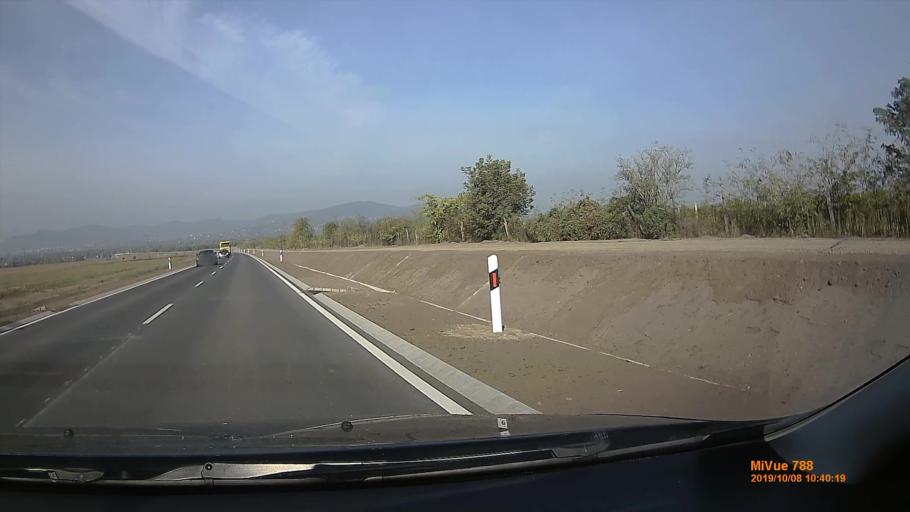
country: HU
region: Pest
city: God
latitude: 47.6611
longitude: 19.1474
